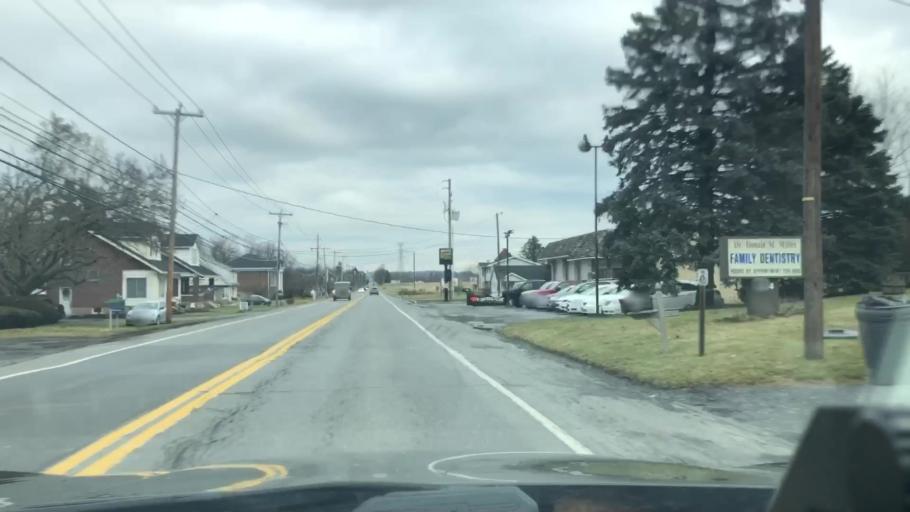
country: US
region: Pennsylvania
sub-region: Northampton County
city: Nazareth
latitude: 40.7143
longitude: -75.3234
